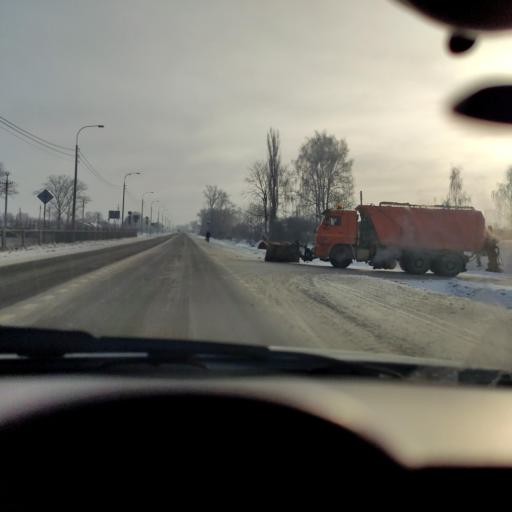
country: RU
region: Kursk
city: Kursk
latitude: 51.7071
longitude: 36.4843
